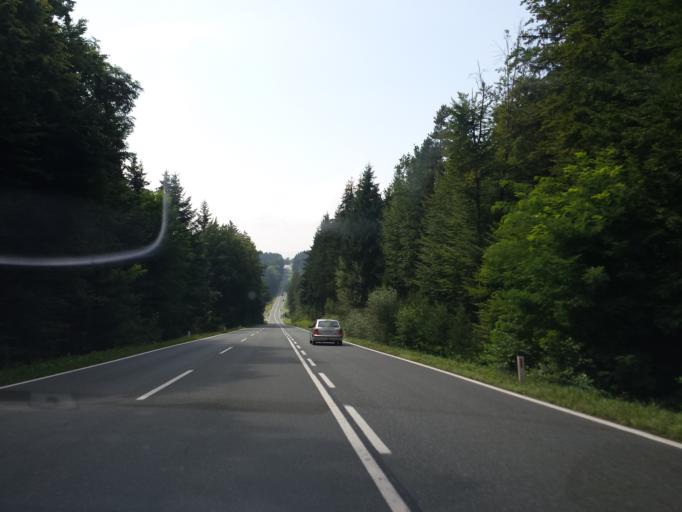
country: AT
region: Styria
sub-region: Politischer Bezirk Deutschlandsberg
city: Rassach
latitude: 46.8478
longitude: 15.2717
